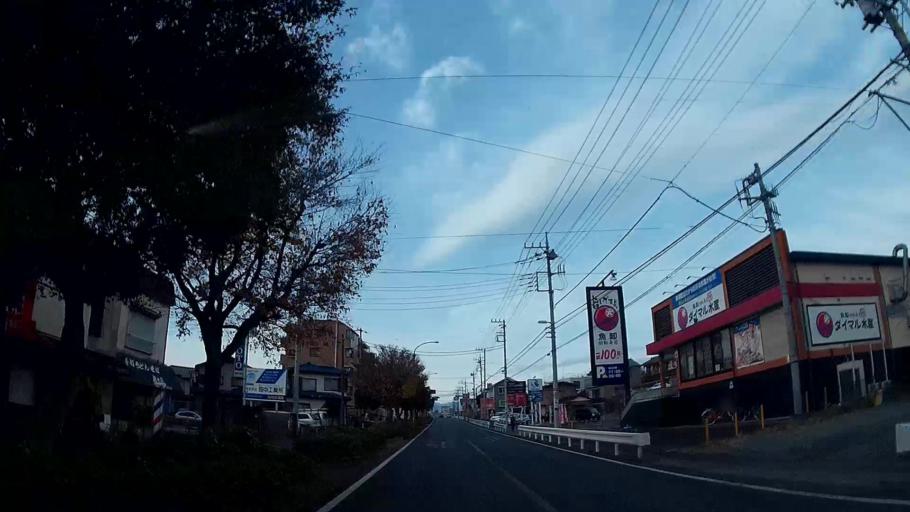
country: JP
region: Saitama
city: Hanno
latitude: 35.8455
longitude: 139.3488
